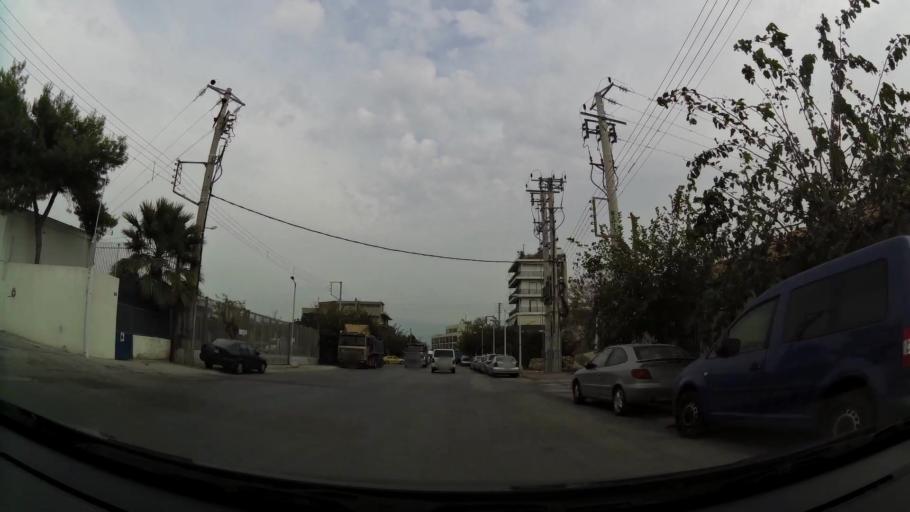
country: GR
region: Attica
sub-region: Nomarchia Athinas
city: Tavros
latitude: 37.9728
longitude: 23.6892
